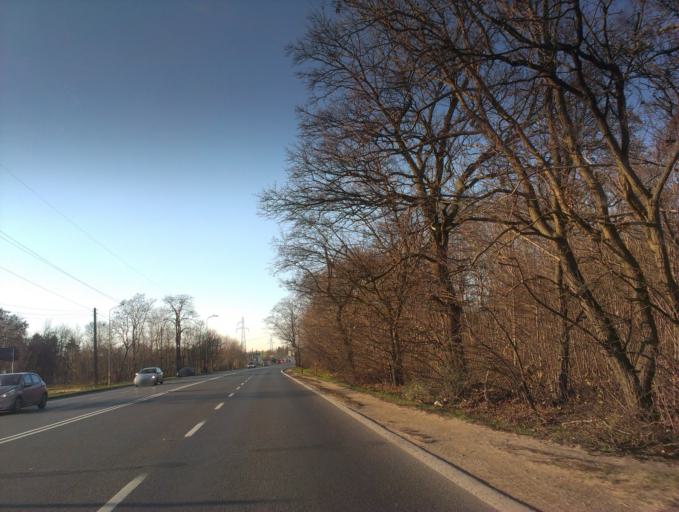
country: PL
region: Greater Poland Voivodeship
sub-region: Poznan
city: Poznan
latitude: 52.4430
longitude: 16.9190
